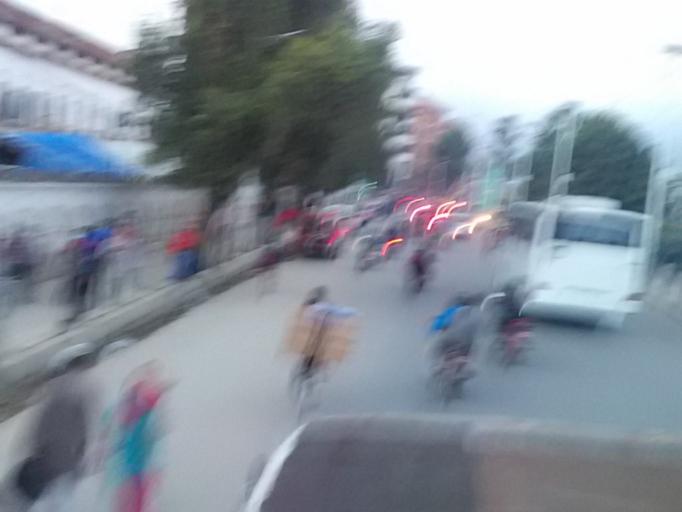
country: NP
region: Central Region
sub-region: Bagmati Zone
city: Kathmandu
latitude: 27.7071
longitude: 85.3143
